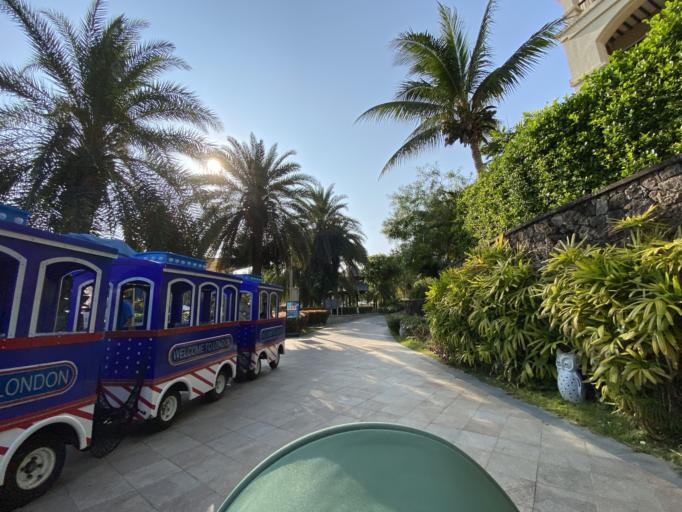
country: CN
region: Hainan
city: Haitangwan
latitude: 18.3494
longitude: 109.7390
